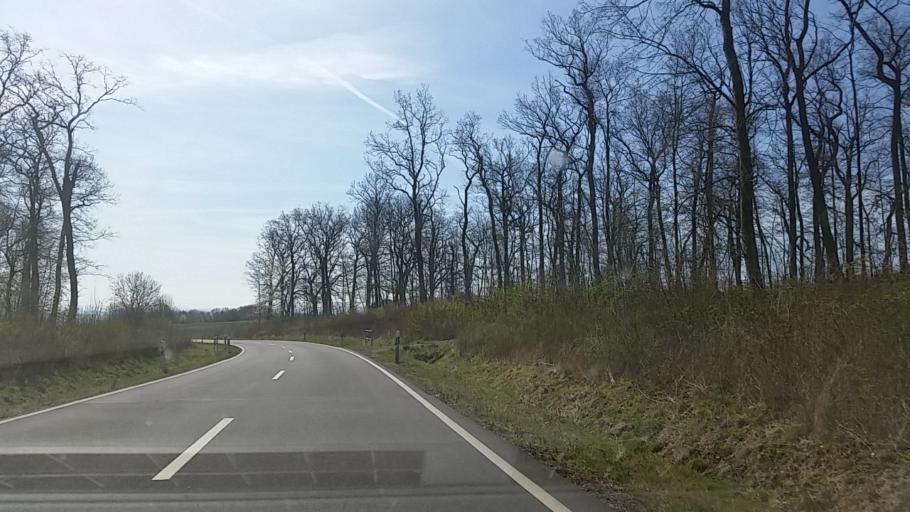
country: DE
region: Lower Saxony
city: Twieflingen
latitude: 52.1493
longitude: 10.9363
